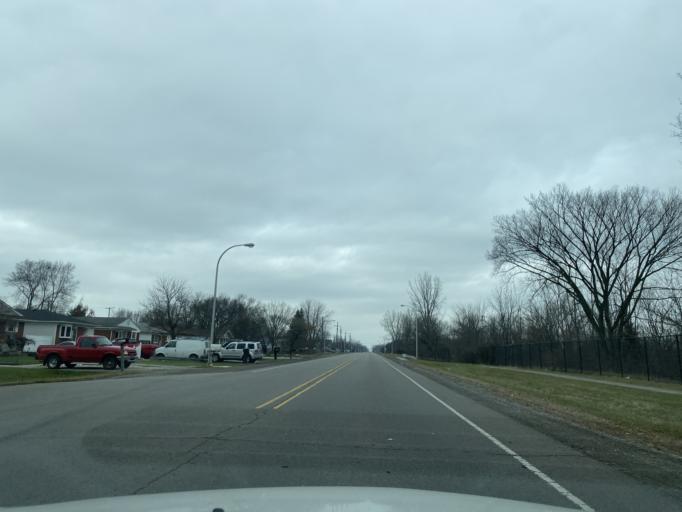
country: US
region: Michigan
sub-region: Wayne County
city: Taylor
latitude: 42.2043
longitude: -83.2874
